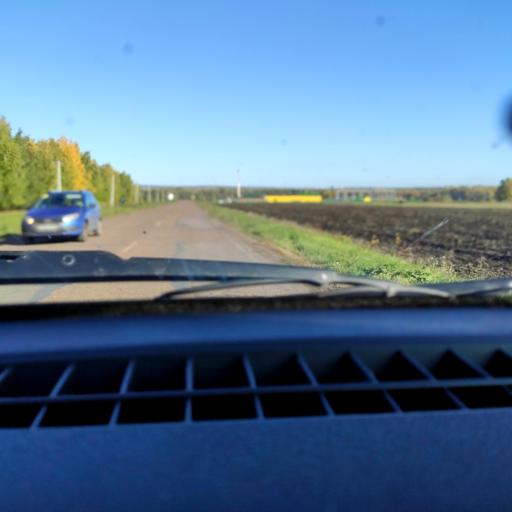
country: RU
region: Bashkortostan
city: Avdon
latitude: 54.5971
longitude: 55.7995
